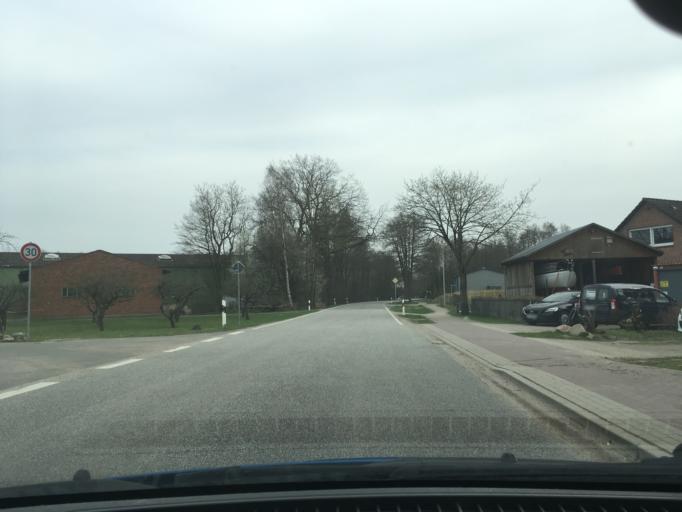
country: DE
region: Lower Saxony
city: Tespe
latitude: 53.3929
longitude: 10.4268
